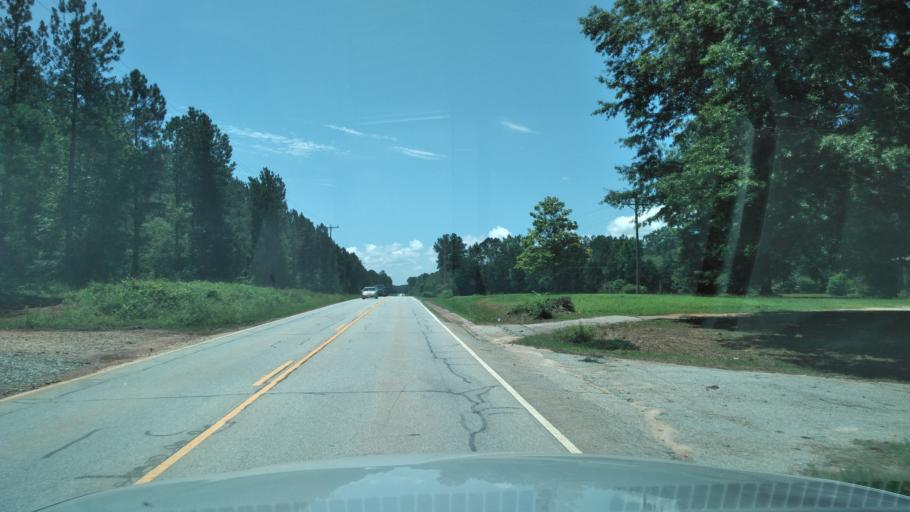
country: US
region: South Carolina
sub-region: Laurens County
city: Laurens
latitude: 34.3852
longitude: -82.0524
